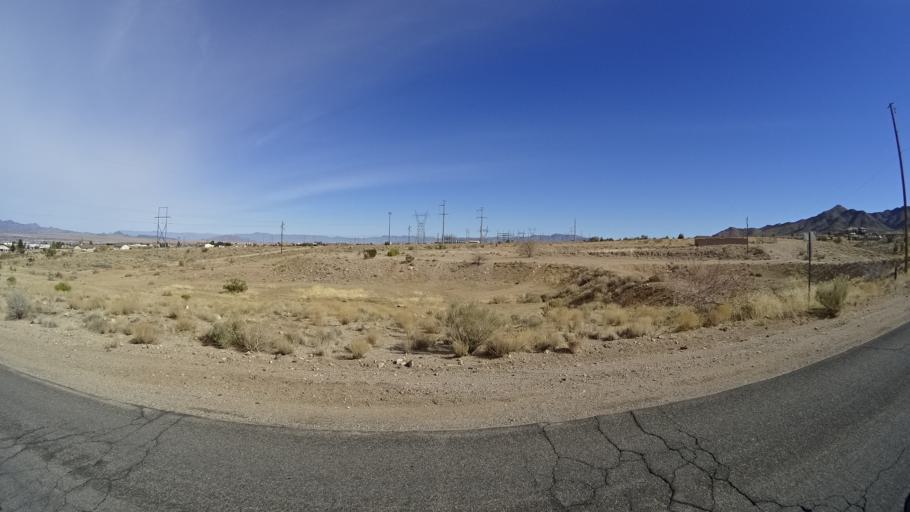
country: US
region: Arizona
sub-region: Mohave County
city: Kingman
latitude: 35.1737
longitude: -113.9851
